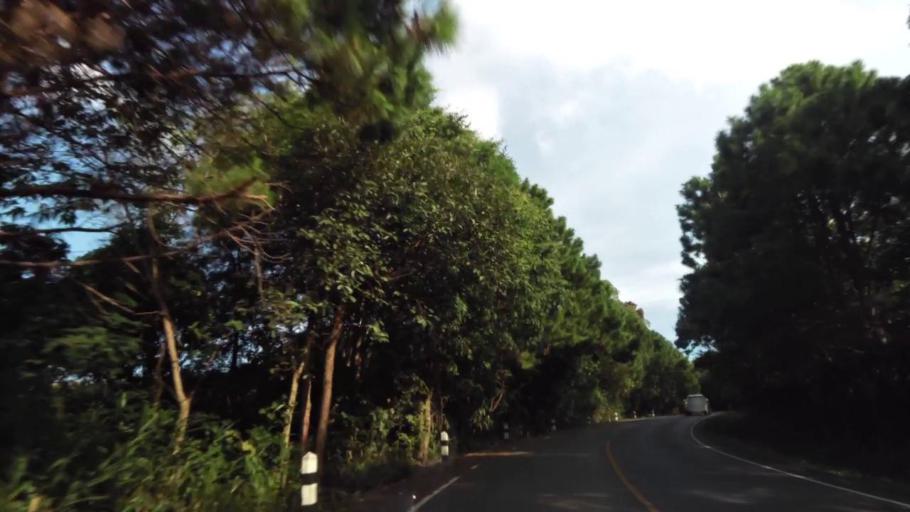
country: TH
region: Chiang Rai
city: Khun Tan
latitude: 19.8707
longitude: 100.3257
